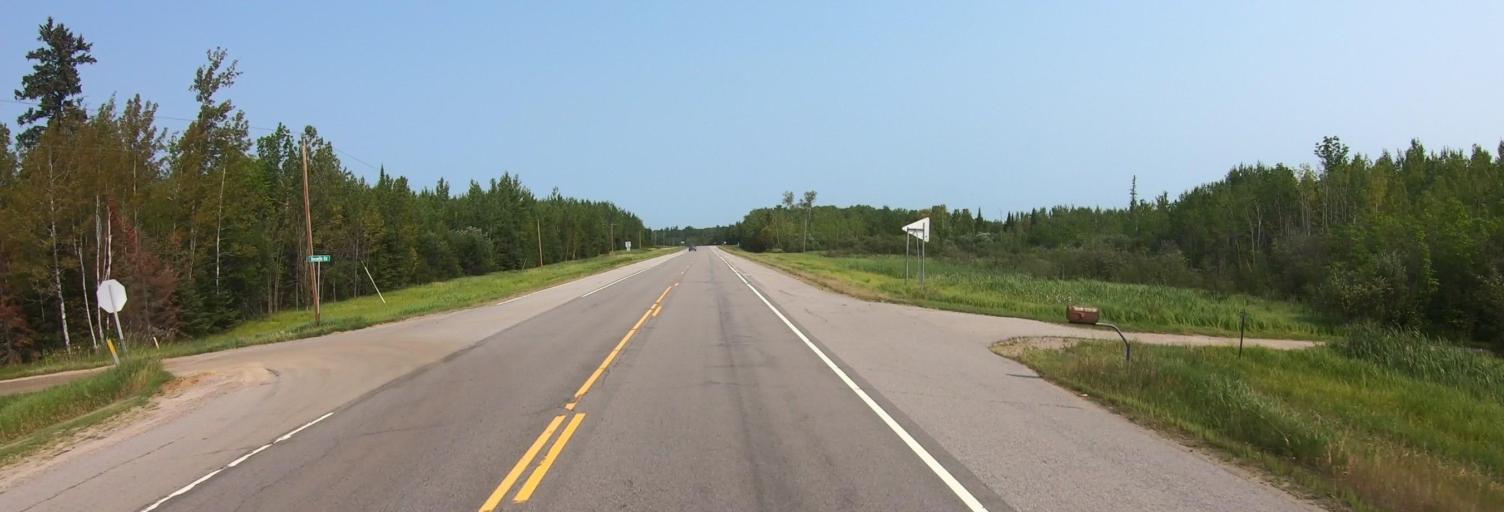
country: US
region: Minnesota
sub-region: Saint Louis County
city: Mountain Iron
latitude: 48.0791
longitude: -92.8221
